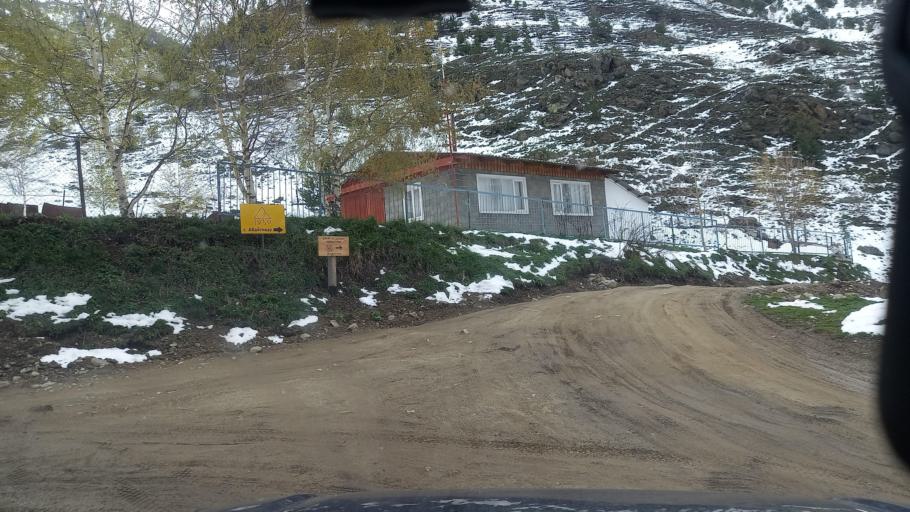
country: RU
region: North Ossetia
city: Mizur
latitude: 42.8052
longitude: 43.9465
